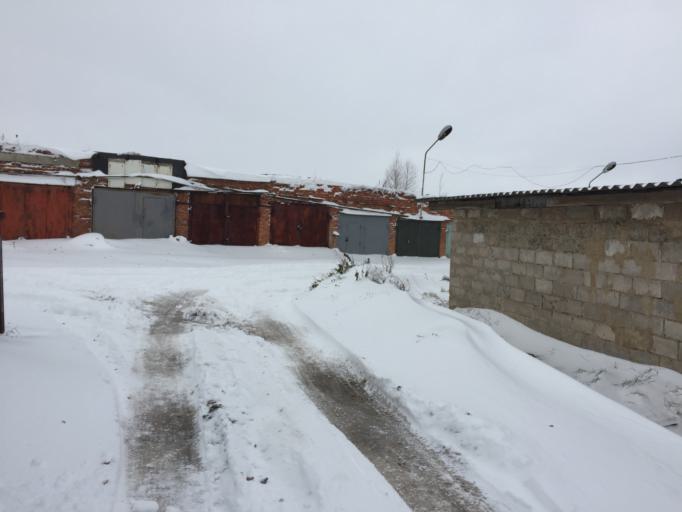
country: RU
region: Tula
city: Shchekino
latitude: 53.8532
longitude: 37.4763
